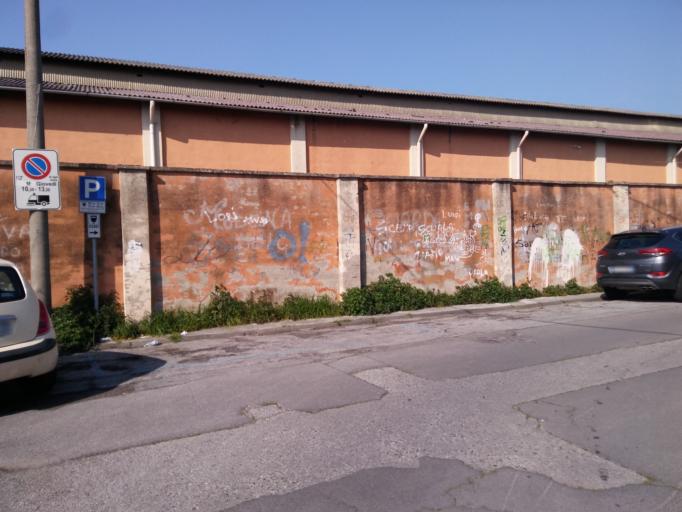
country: IT
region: Tuscany
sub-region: Provincia di Lucca
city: Viareggio
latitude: 43.8643
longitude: 10.2555
